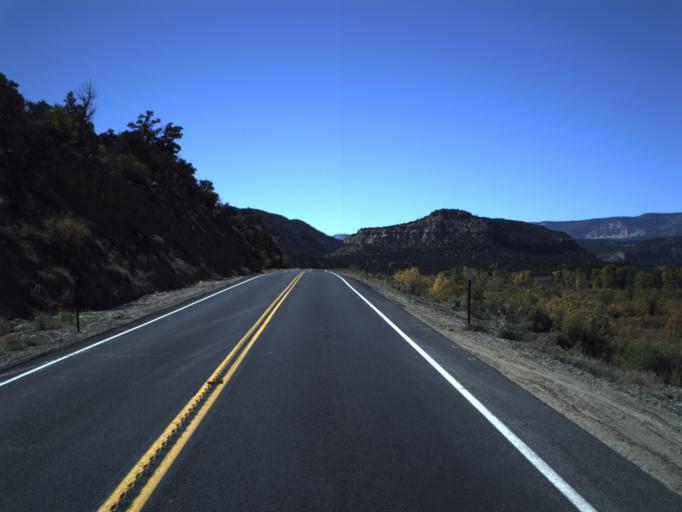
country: US
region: Utah
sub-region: Wayne County
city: Loa
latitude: 37.7644
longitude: -111.6848
